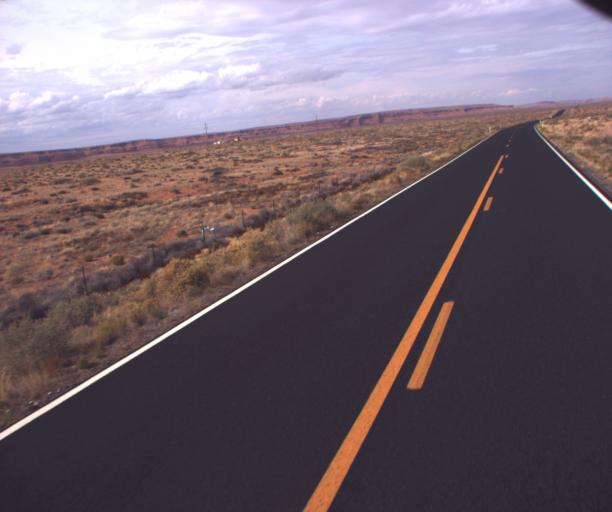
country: US
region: Arizona
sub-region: Apache County
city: Many Farms
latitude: 36.5616
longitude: -109.5406
